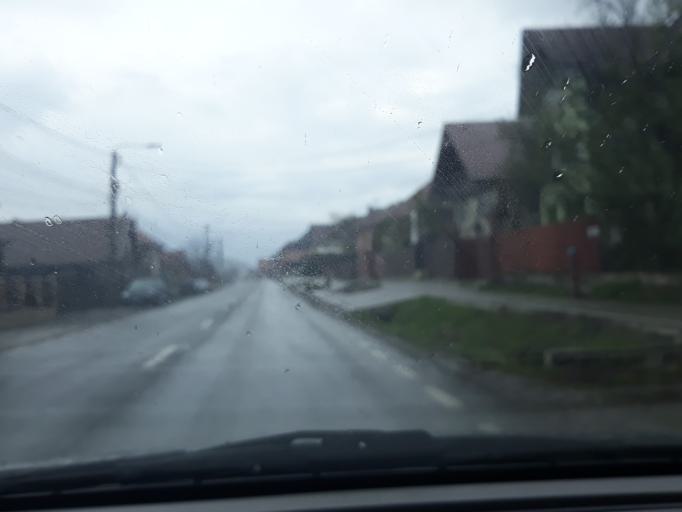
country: RO
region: Harghita
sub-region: Comuna Corund
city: Corund
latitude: 46.4763
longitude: 25.1765
